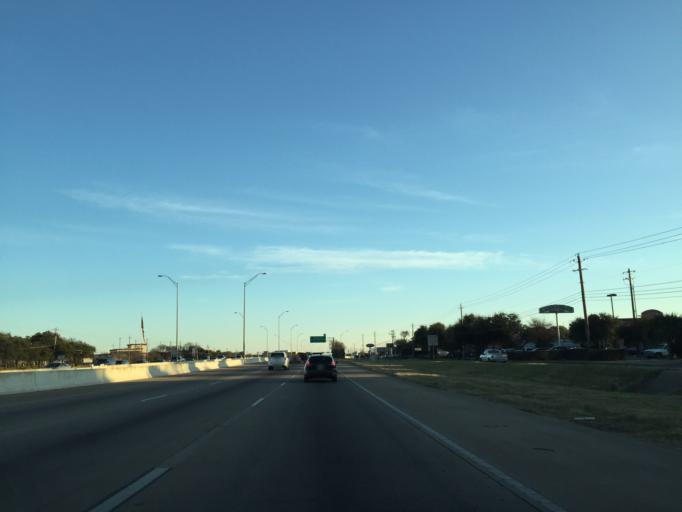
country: US
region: Texas
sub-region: Williamson County
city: Jollyville
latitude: 30.4162
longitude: -97.7465
